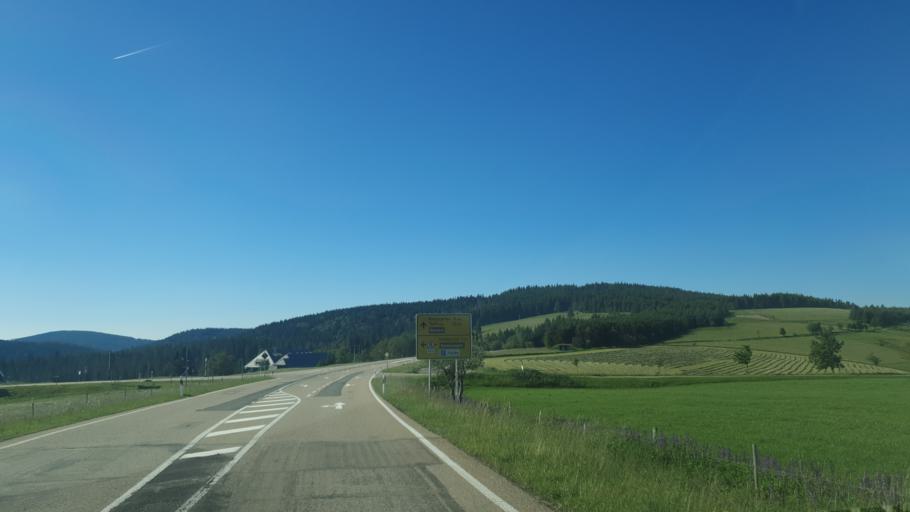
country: DE
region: Baden-Wuerttemberg
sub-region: Freiburg Region
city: Horben
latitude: 47.8943
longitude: 7.8910
